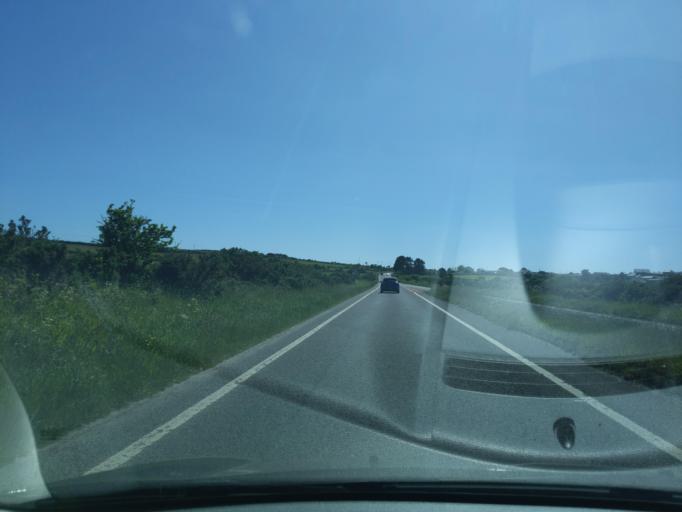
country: GB
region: England
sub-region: Cornwall
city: Penryn
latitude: 50.1672
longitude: -5.1504
